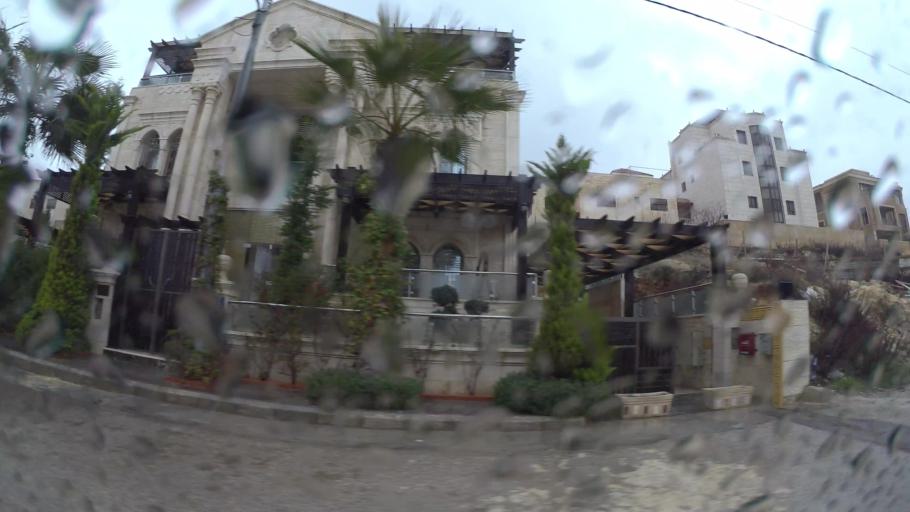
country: JO
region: Amman
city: Al Jubayhah
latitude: 32.0091
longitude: 35.8999
